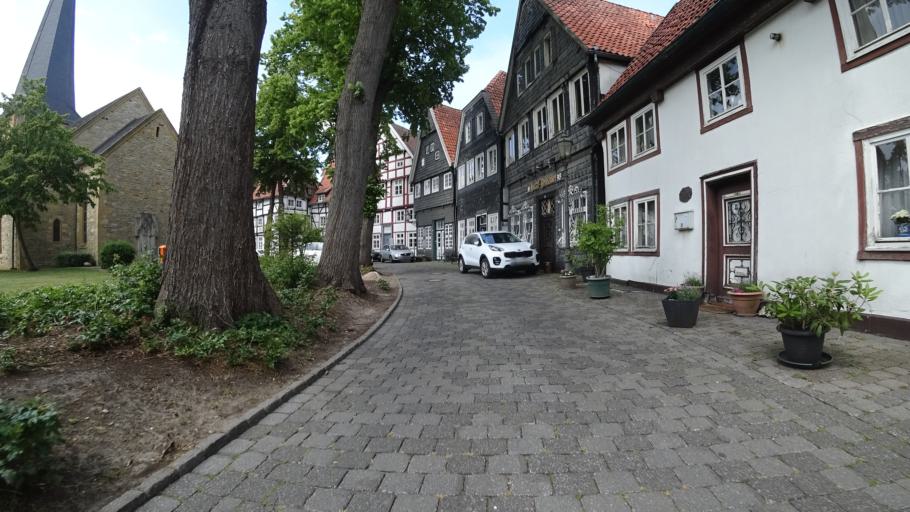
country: DE
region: North Rhine-Westphalia
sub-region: Regierungsbezirk Detmold
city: Guetersloh
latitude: 51.9049
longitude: 8.3787
